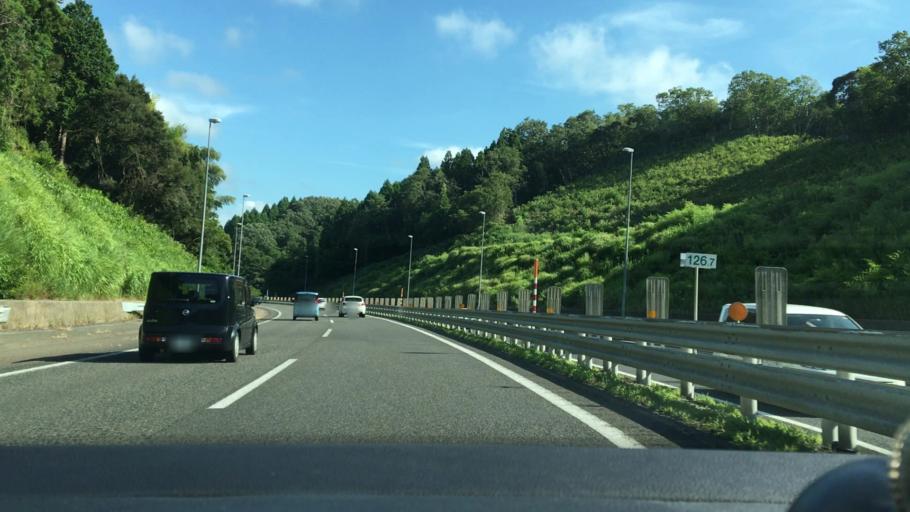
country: JP
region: Fukui
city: Maruoka
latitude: 36.2838
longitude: 136.2772
